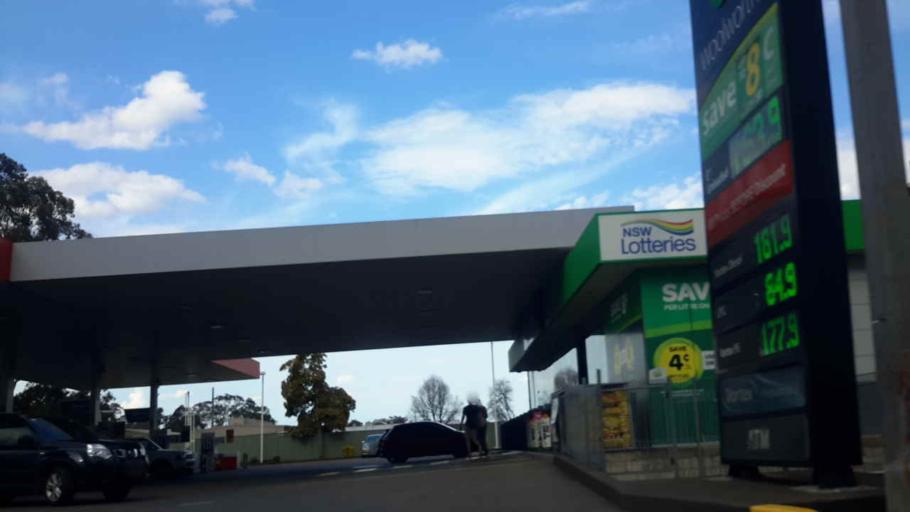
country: AU
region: New South Wales
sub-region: Penrith Municipality
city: Kingswood Park
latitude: -33.7550
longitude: 150.7127
